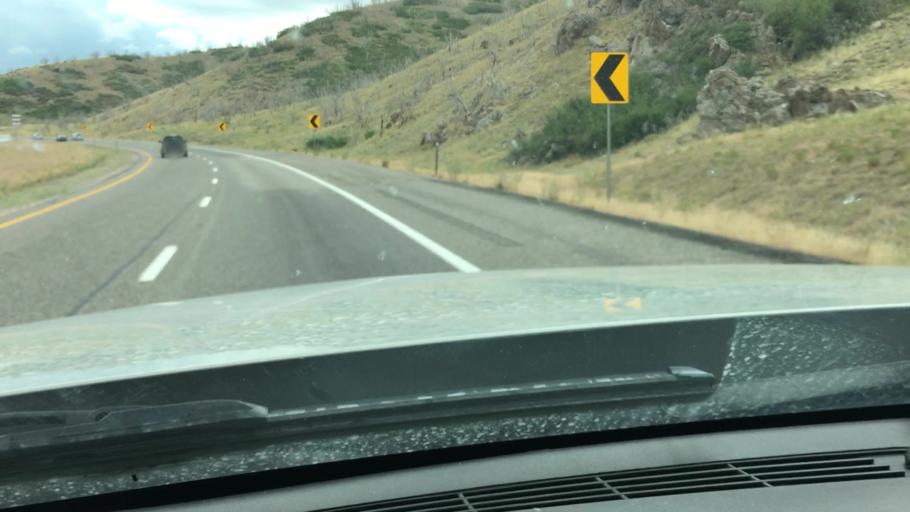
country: US
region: Utah
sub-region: Millard County
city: Fillmore
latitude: 38.6855
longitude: -112.6017
